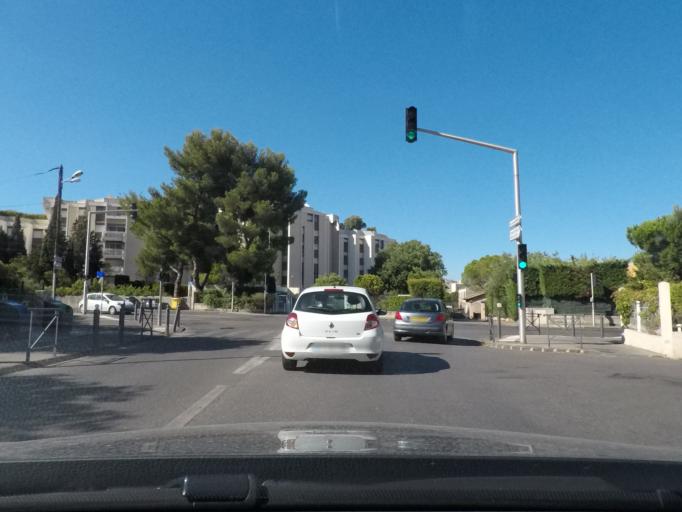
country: FR
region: Provence-Alpes-Cote d'Azur
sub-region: Departement des Bouches-du-Rhone
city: Marseille 09
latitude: 43.2536
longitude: 5.4138
